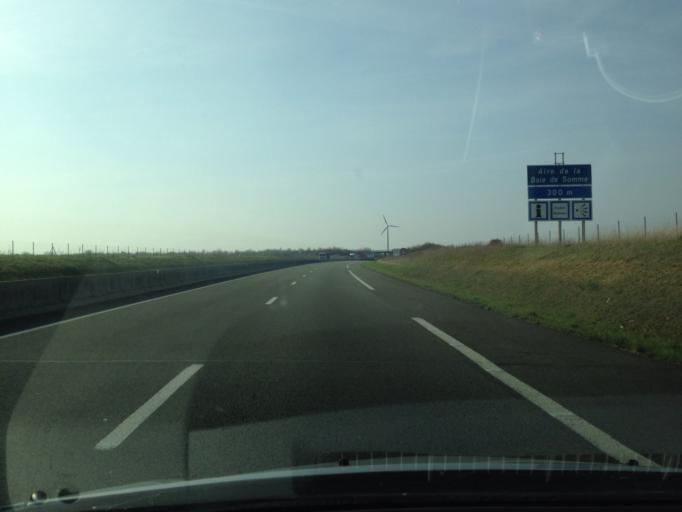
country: FR
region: Picardie
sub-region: Departement de la Somme
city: Sailly-Flibeaucourt
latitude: 50.1644
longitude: 1.7650
